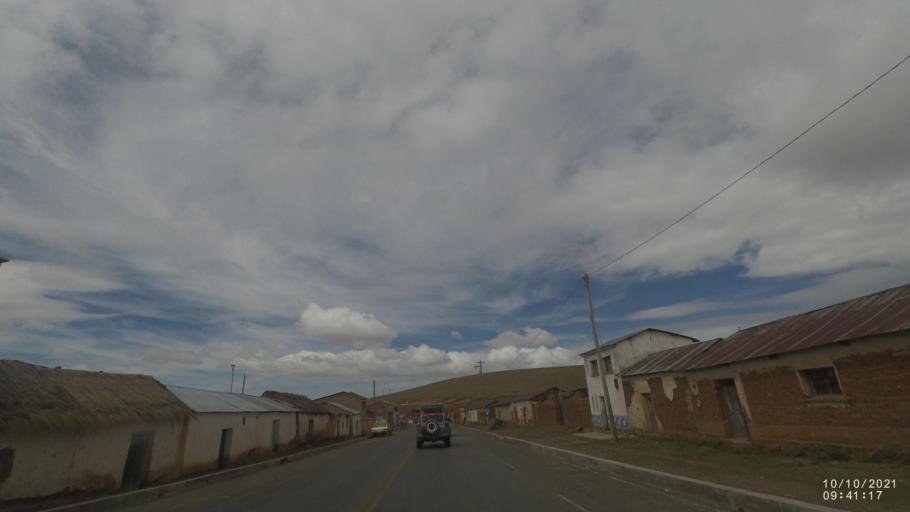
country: BO
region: La Paz
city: Quime
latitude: -17.1464
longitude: -67.3443
